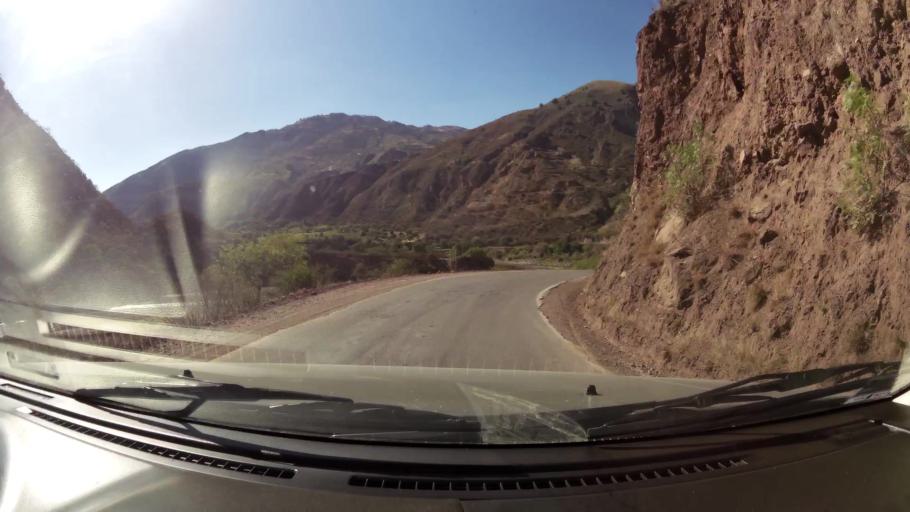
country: PE
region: Huancavelica
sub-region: Provincia de Acobamba
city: Pomacocha
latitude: -12.7748
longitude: -74.4994
